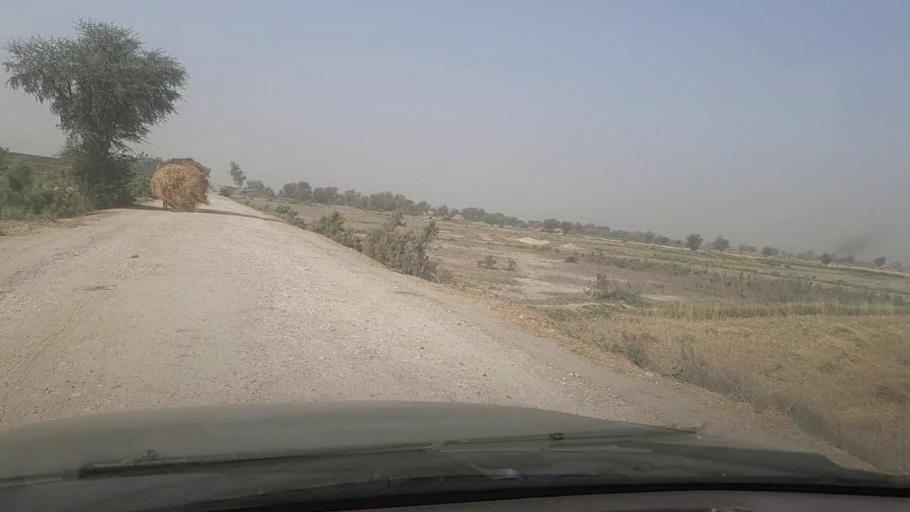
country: PK
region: Sindh
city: Shikarpur
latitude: 27.8984
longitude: 68.5888
